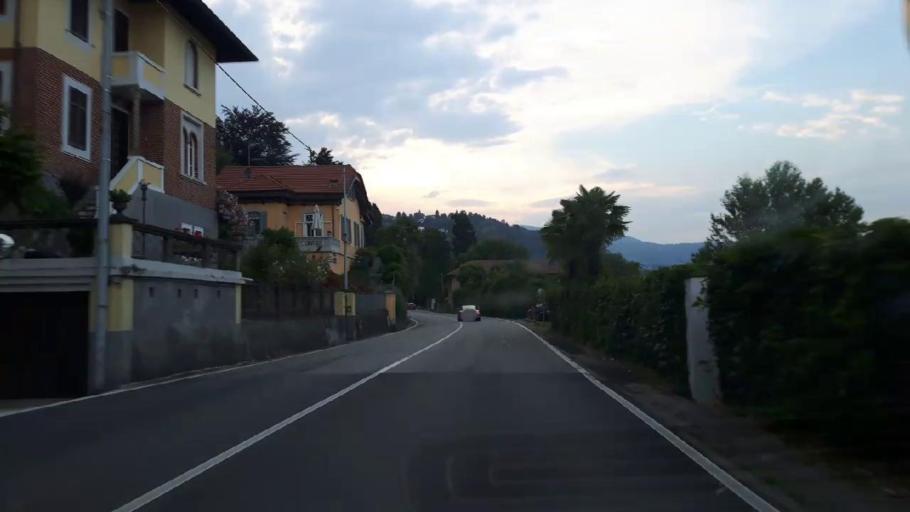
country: IT
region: Piedmont
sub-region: Provincia di Novara
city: Arona
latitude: 45.7694
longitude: 8.5484
